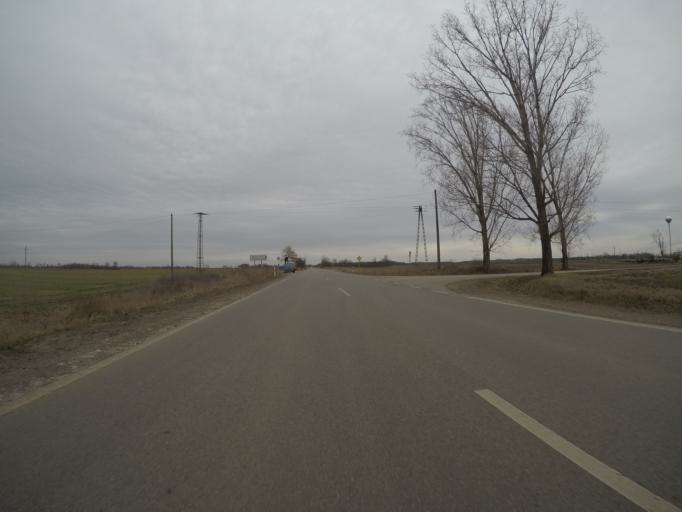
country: HU
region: Jasz-Nagykun-Szolnok
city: Jaszjakohalma
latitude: 47.5170
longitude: 20.0257
